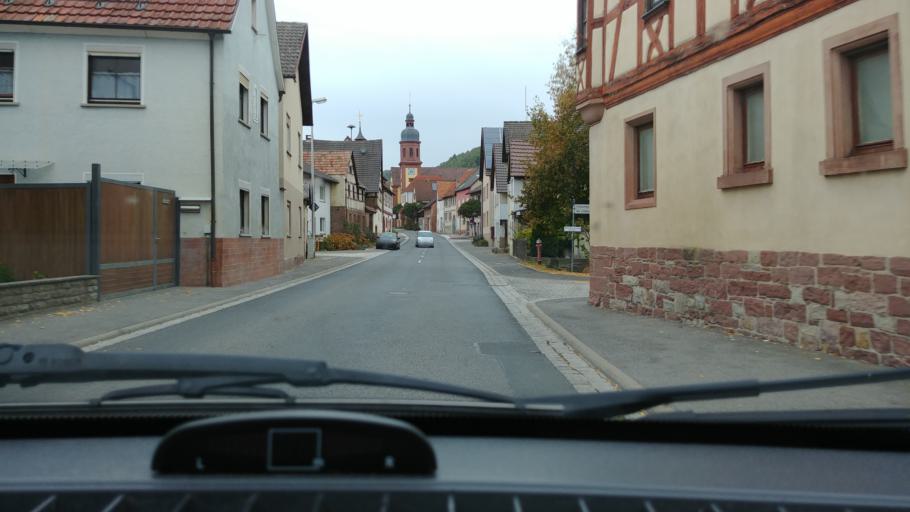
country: DE
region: Bavaria
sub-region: Regierungsbezirk Unterfranken
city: Neubrunn
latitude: 49.7030
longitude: 9.6552
